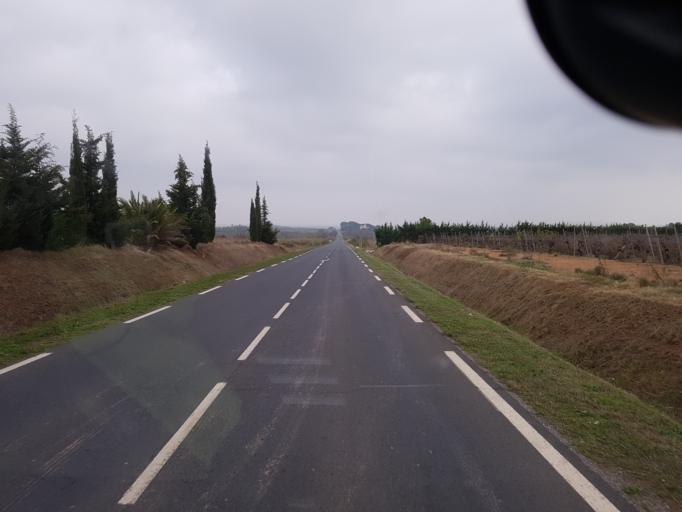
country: FR
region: Languedoc-Roussillon
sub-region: Departement de l'Herault
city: Marseillan
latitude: 43.3770
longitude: 3.5343
